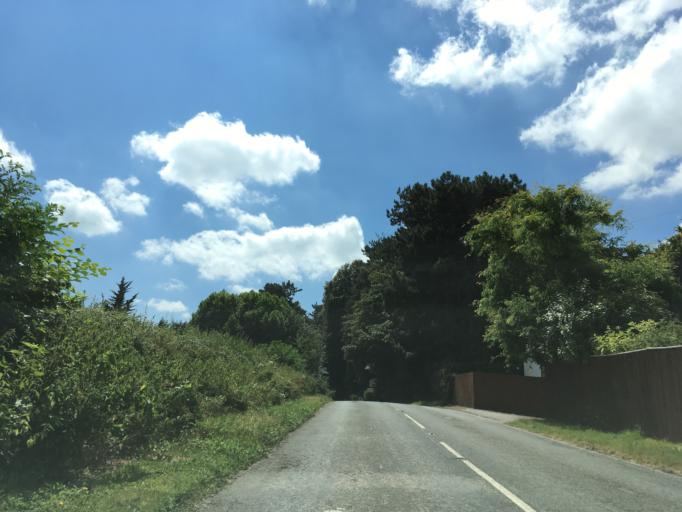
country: GB
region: England
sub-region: Gloucestershire
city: Painswick
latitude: 51.8235
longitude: -2.2081
